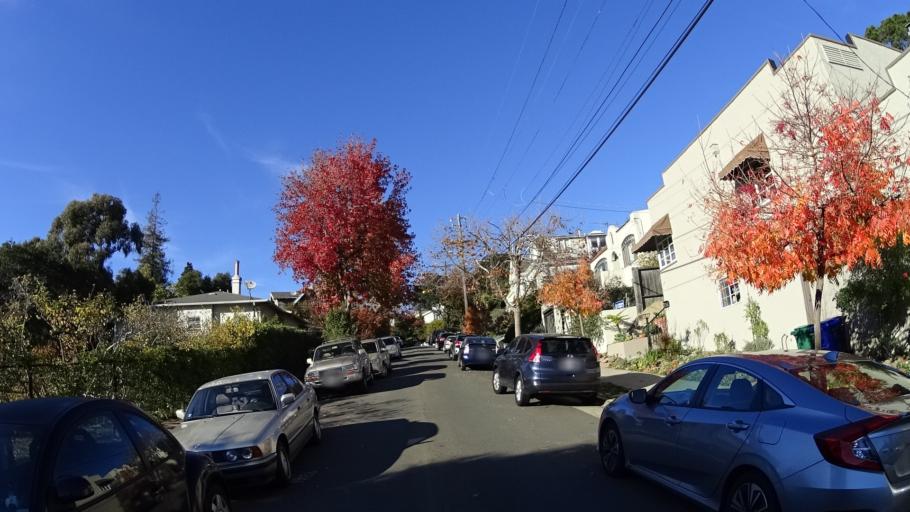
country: US
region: California
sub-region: Alameda County
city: Piedmont
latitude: 37.8225
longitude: -122.2448
